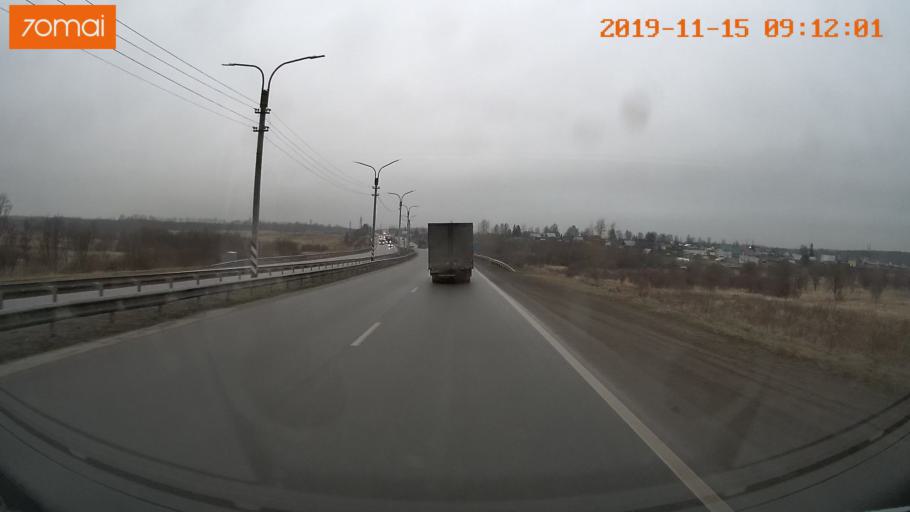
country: RU
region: Vologda
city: Tonshalovo
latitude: 59.2038
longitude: 37.9415
